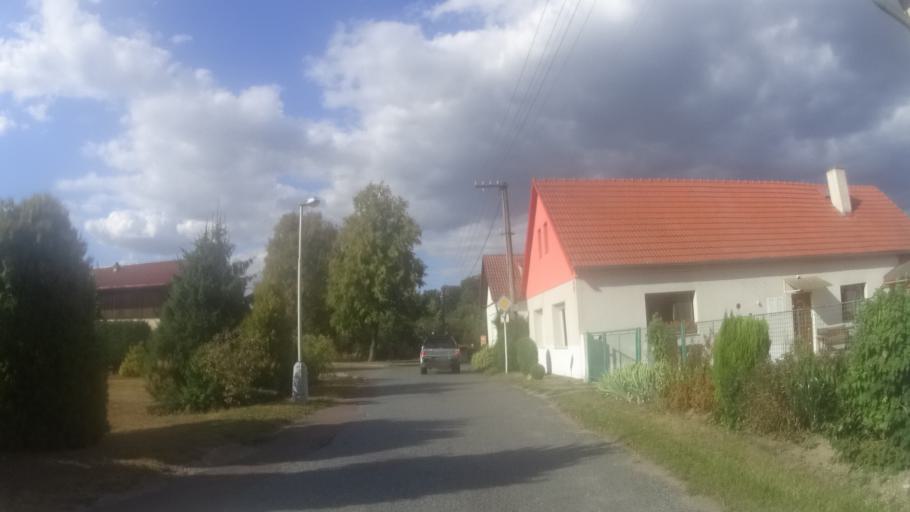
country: CZ
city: Albrechtice nad Orlici
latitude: 50.1724
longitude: 16.0326
